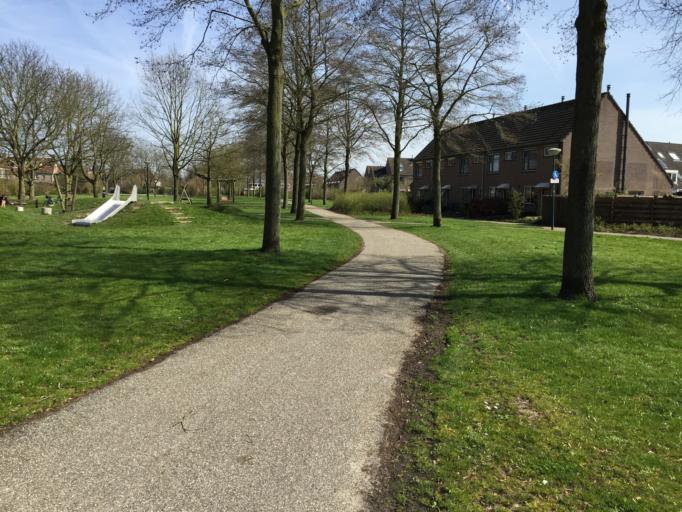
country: NL
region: Utrecht
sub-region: Gemeente Zeist
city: Zeist
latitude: 52.0544
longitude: 5.2349
